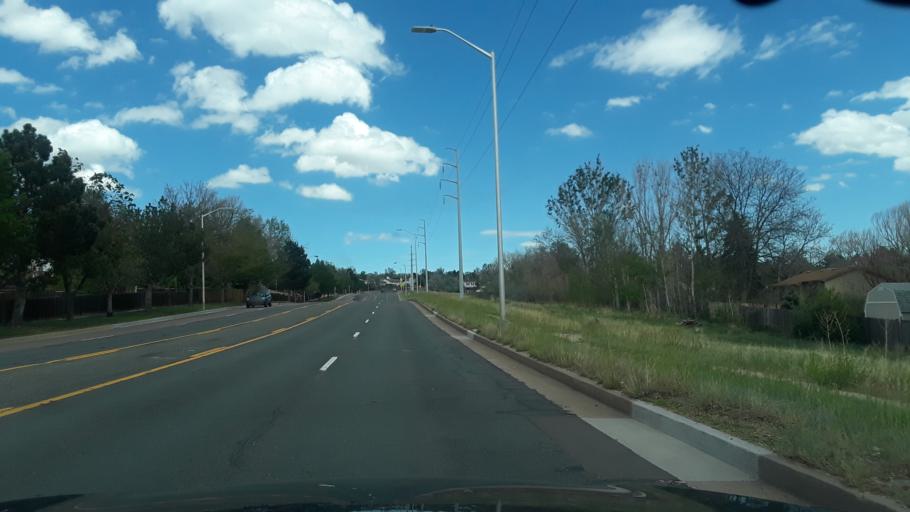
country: US
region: Colorado
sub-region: El Paso County
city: Air Force Academy
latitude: 38.9442
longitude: -104.7891
